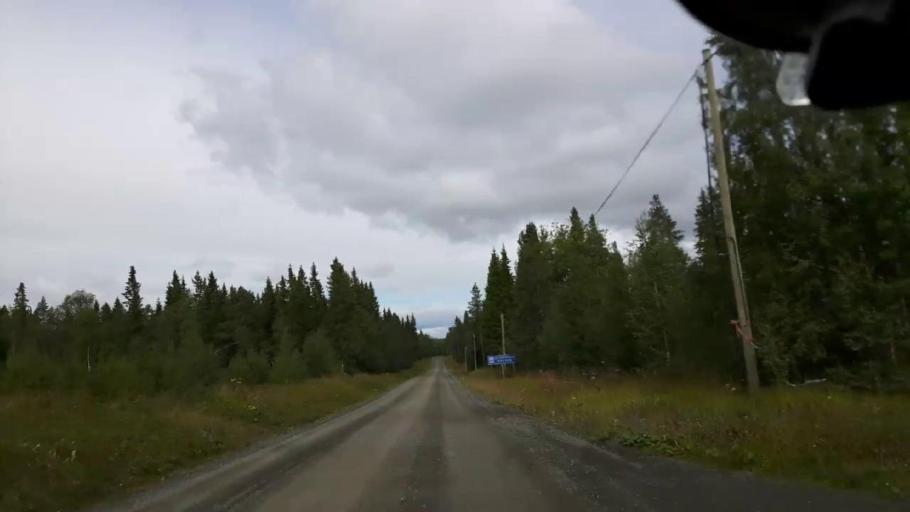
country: SE
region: Jaemtland
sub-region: Krokoms Kommun
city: Valla
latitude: 63.3942
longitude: 14.1024
